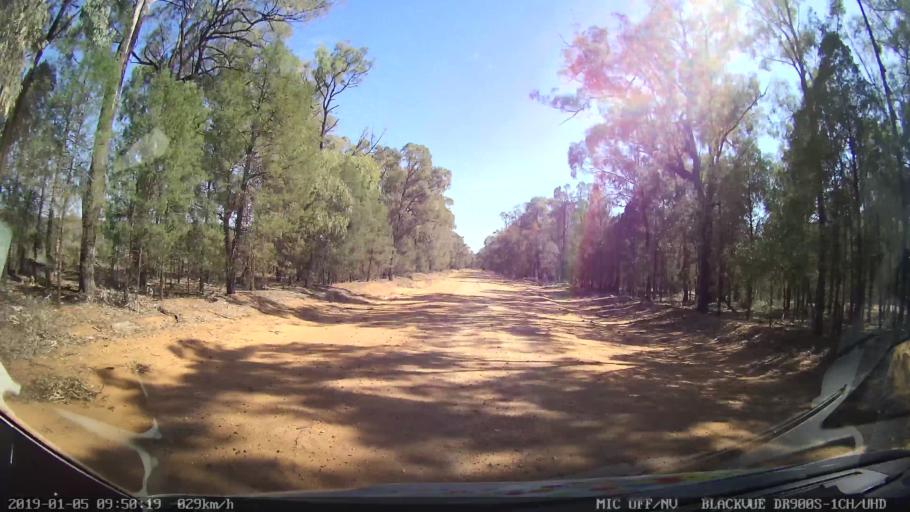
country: AU
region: New South Wales
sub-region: Gilgandra
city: Gilgandra
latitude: -31.6651
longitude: 148.7588
